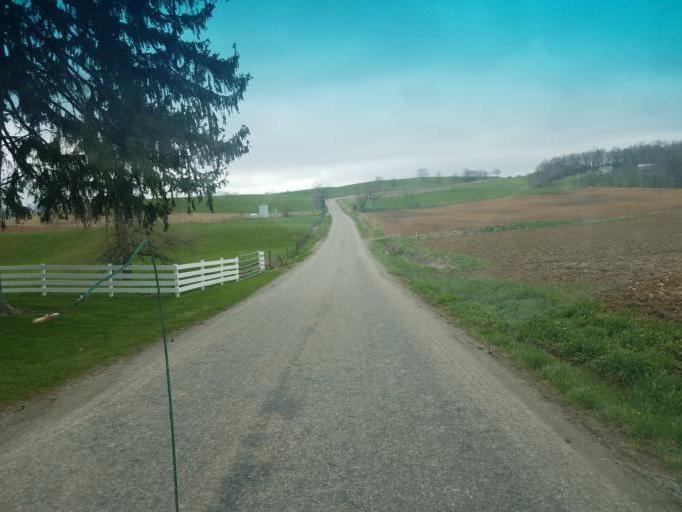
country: US
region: Ohio
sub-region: Stark County
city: Beach City
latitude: 40.6259
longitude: -81.6665
